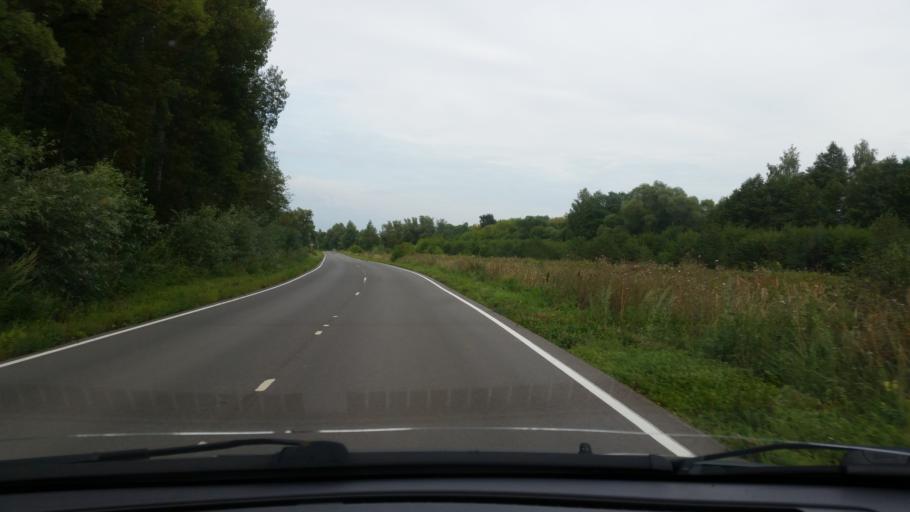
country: RU
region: Moskovskaya
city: Bol'shoye Gryzlovo
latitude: 54.8471
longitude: 37.7189
